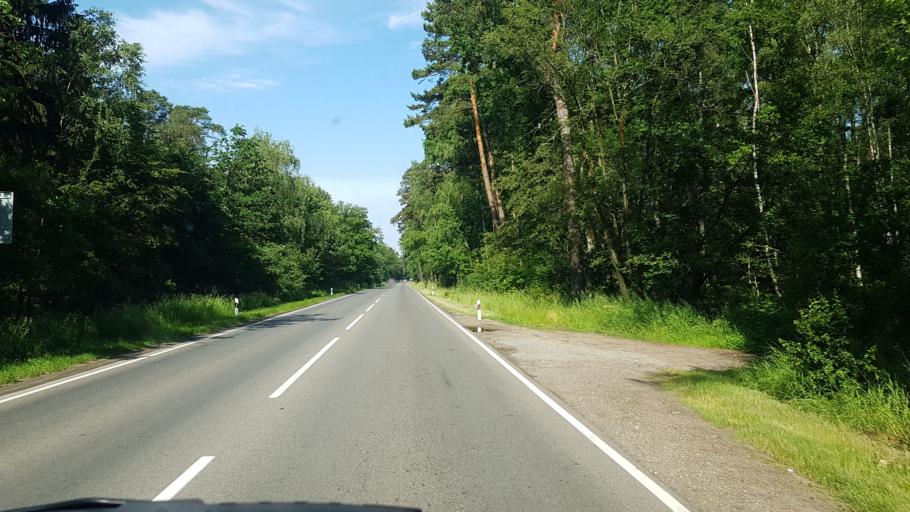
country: RU
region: Kaliningrad
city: Vzmorye
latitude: 54.7047
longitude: 20.2967
